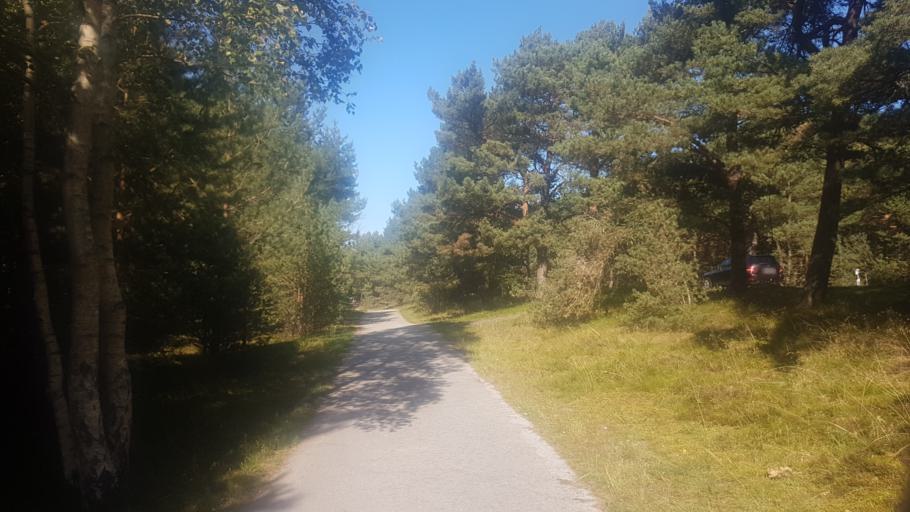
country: DE
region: Mecklenburg-Vorpommern
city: Altenkirchen
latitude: 54.6074
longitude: 13.3817
